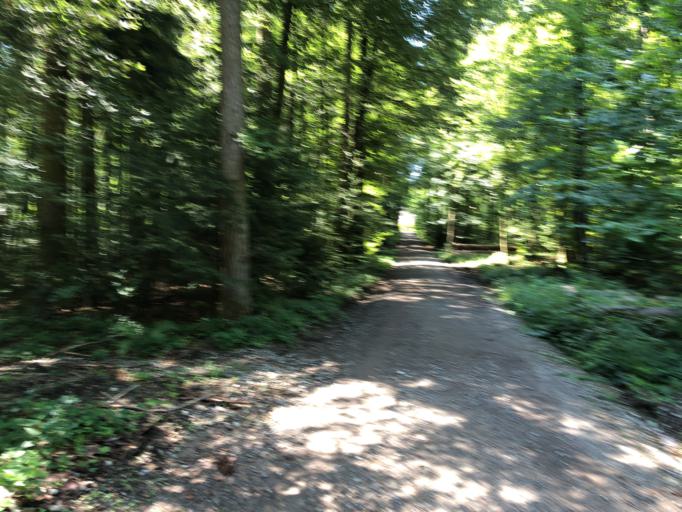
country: CH
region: Zurich
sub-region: Bezirk Uster
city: Pfaffhausen
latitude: 47.3688
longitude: 8.6236
